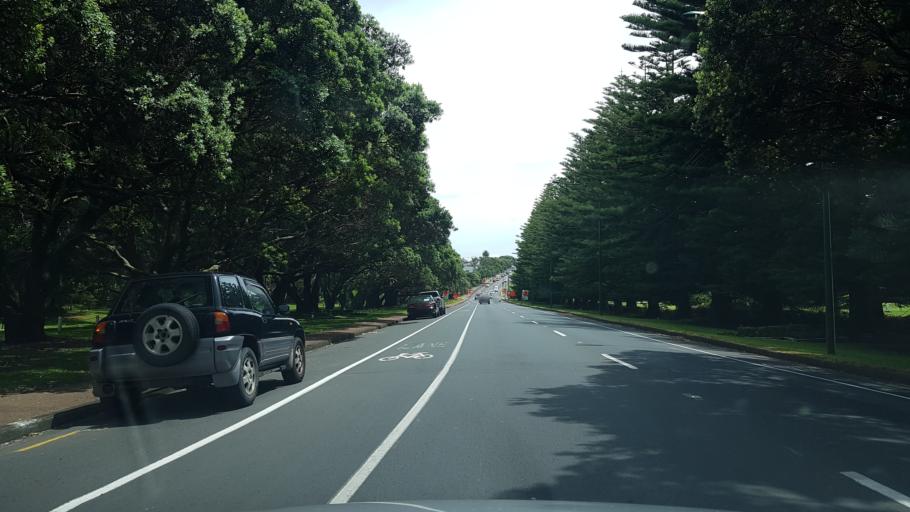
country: NZ
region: Auckland
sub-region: Auckland
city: North Shore
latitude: -36.8200
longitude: 174.7960
